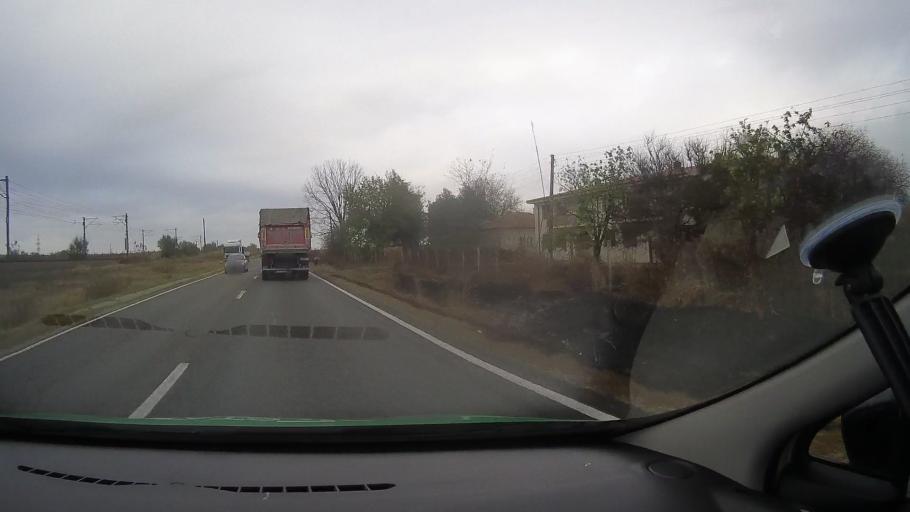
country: RO
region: Constanta
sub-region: Comuna Poarta Alba
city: Poarta Alba
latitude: 44.2265
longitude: 28.3822
